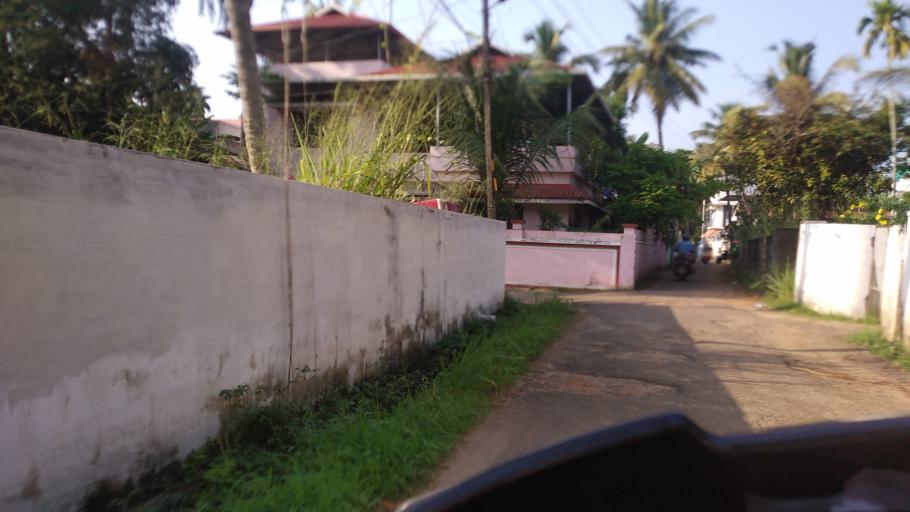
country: IN
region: Kerala
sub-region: Ernakulam
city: Elur
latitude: 10.0517
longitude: 76.2183
